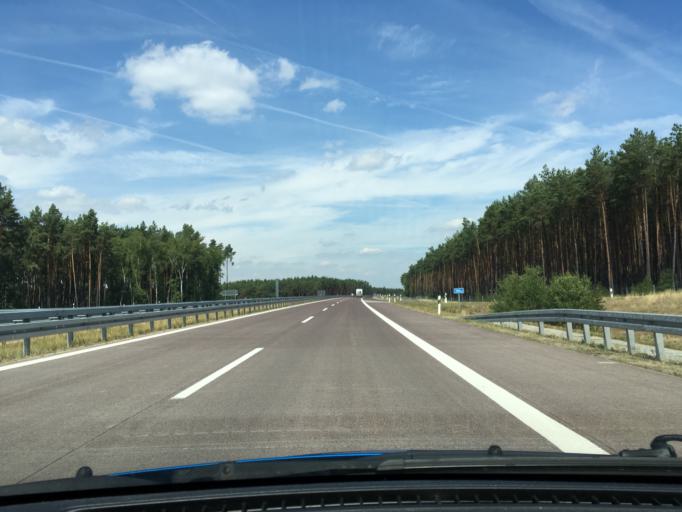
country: DE
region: Mecklenburg-Vorpommern
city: Ludwigslust
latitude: 53.3455
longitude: 11.5189
